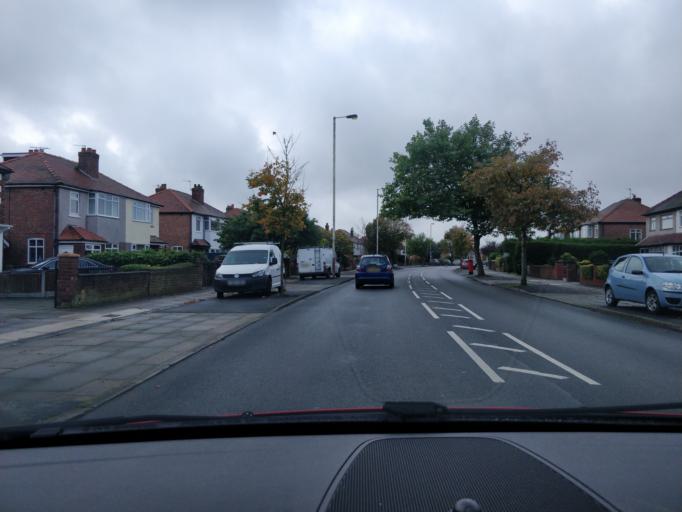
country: GB
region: England
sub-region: Sefton
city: Southport
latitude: 53.6131
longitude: -3.0129
